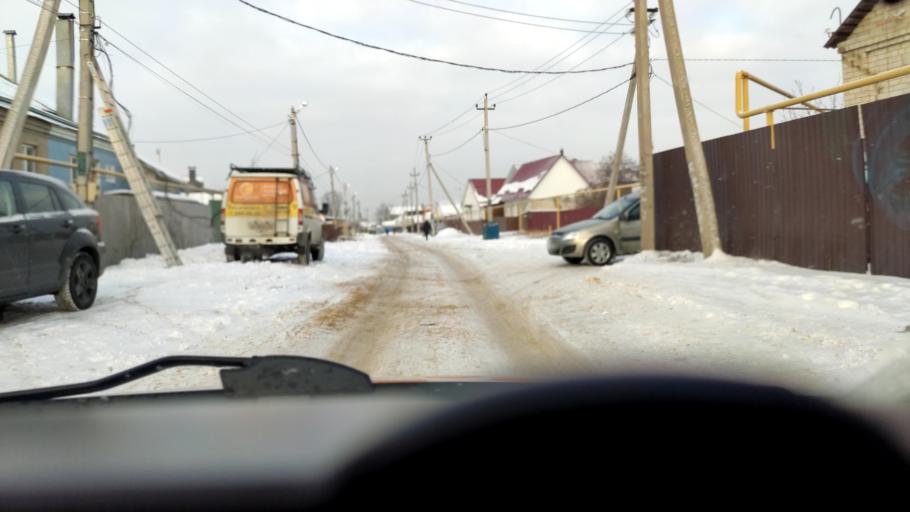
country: RU
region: Voronezj
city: Podgornoye
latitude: 51.7278
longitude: 39.1538
